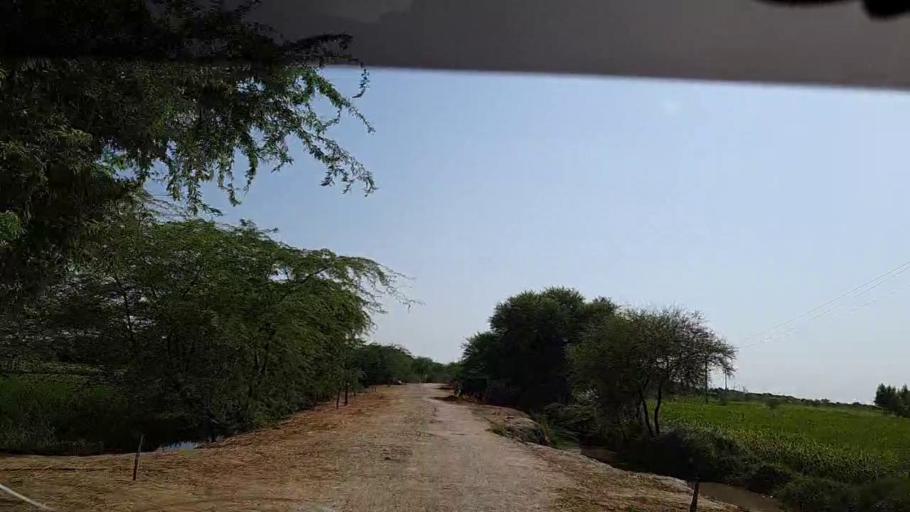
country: PK
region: Sindh
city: Badin
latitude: 24.6349
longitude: 68.7864
